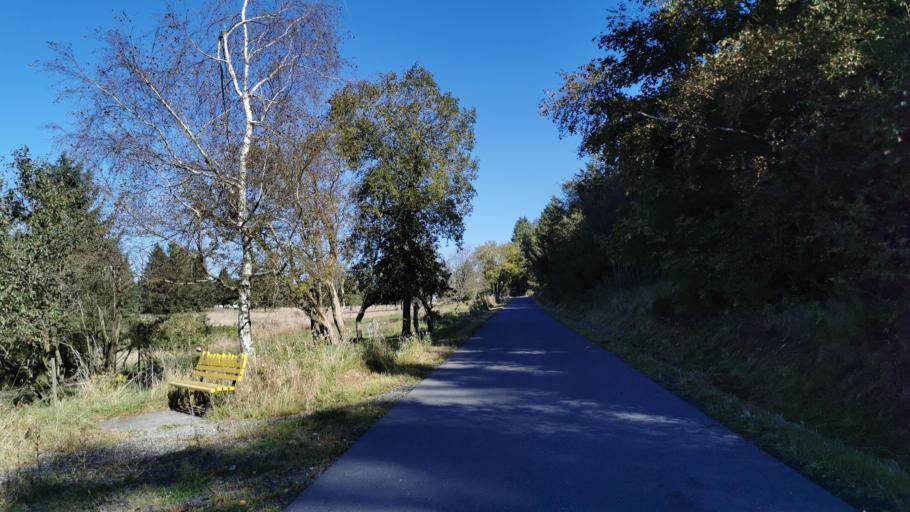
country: DE
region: Bavaria
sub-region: Upper Franconia
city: Tettau
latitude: 50.4795
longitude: 11.2944
